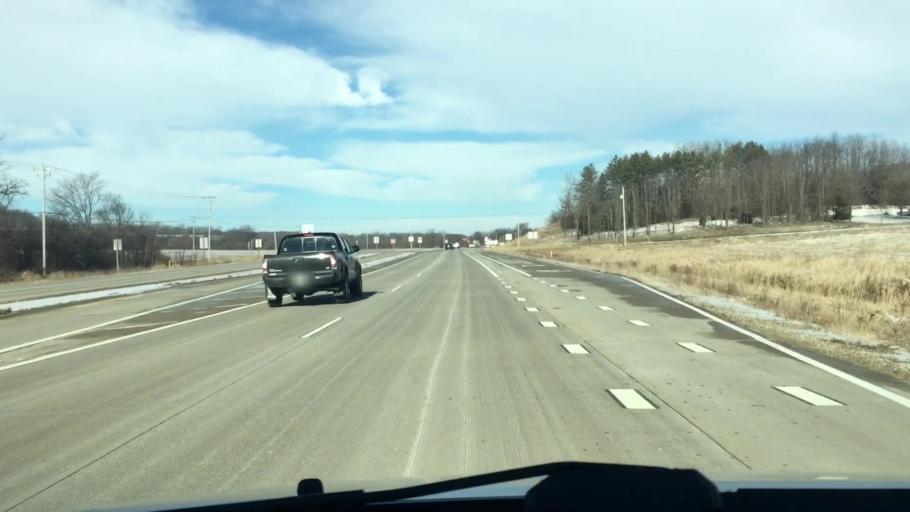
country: US
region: Wisconsin
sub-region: Waukesha County
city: Mukwonago
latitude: 42.8991
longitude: -88.3445
